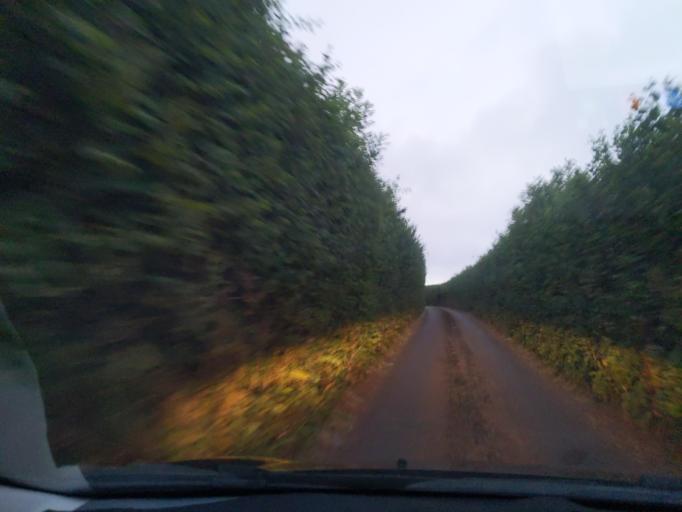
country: GB
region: England
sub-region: Devon
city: Marldon
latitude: 50.4629
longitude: -3.6065
